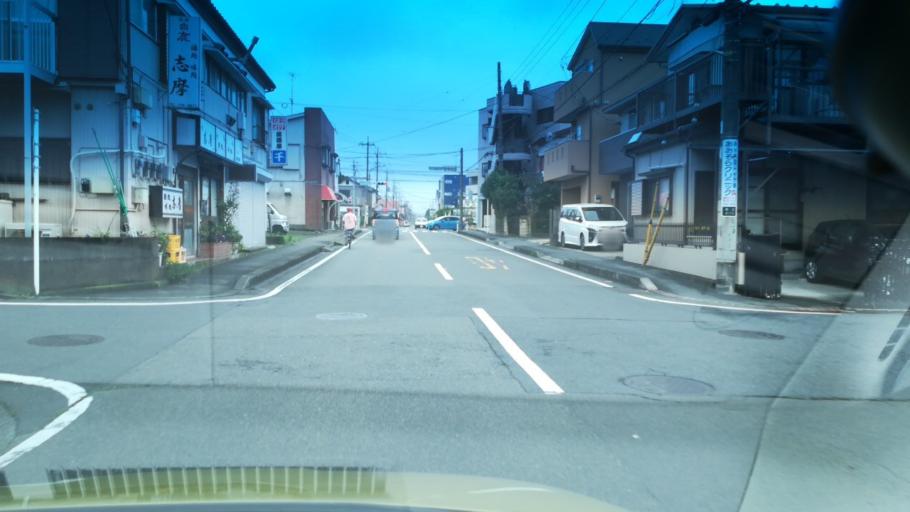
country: JP
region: Tokyo
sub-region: Machida-shi
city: Machida
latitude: 35.5628
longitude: 139.3827
